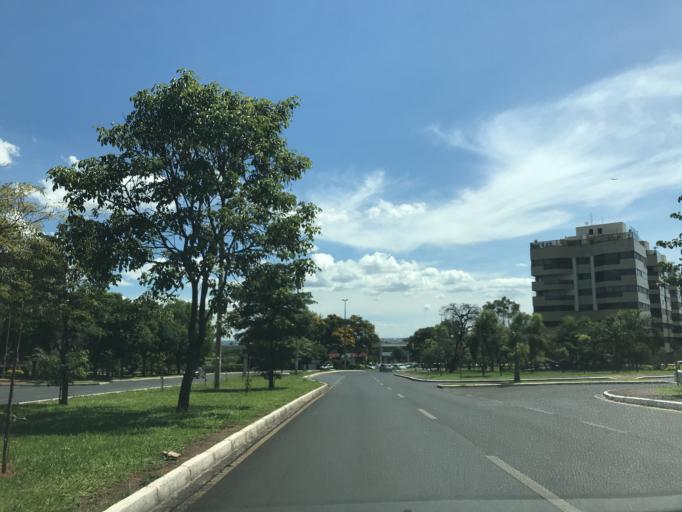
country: BR
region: Federal District
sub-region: Brasilia
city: Brasilia
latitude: -15.8051
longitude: -47.9323
